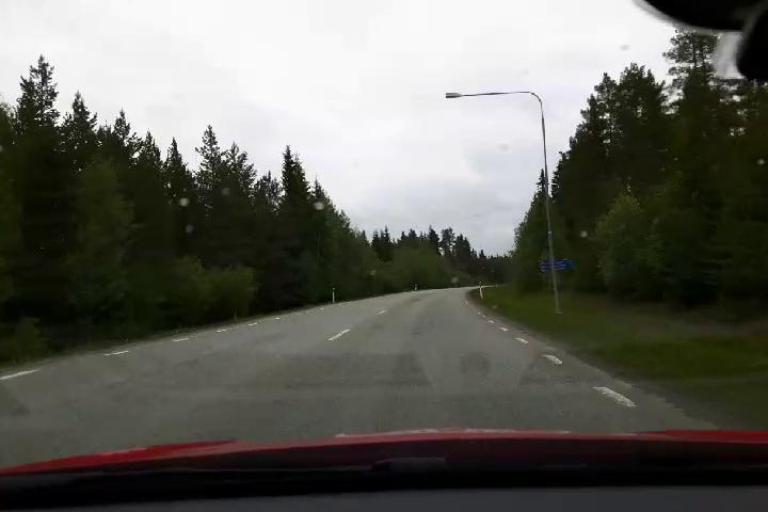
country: SE
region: Jaemtland
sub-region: Bergs Kommun
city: Hoverberg
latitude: 62.6535
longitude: 14.3746
